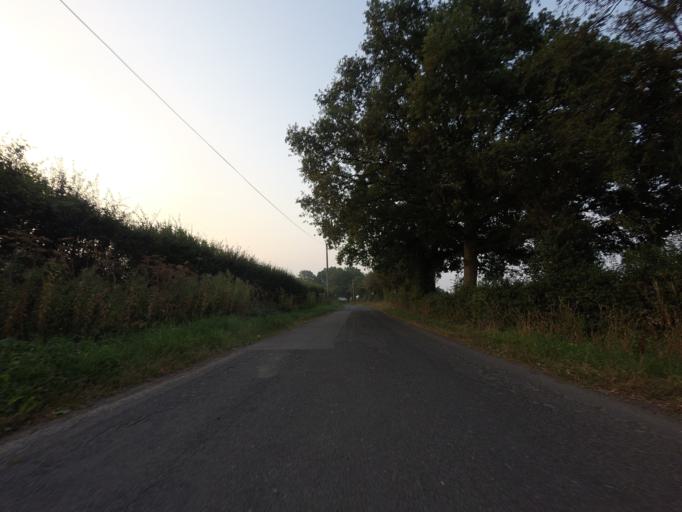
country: GB
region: England
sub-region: Kent
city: Headcorn
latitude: 51.1845
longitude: 0.6608
